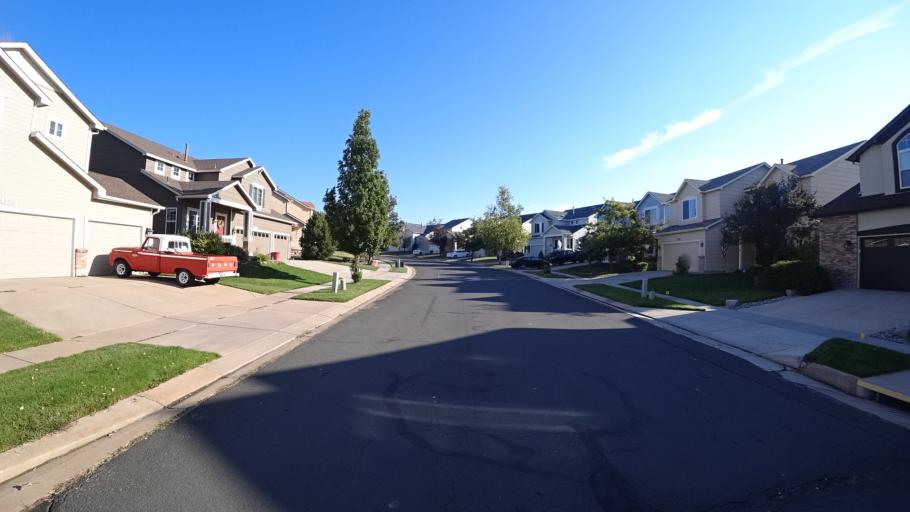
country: US
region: Colorado
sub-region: El Paso County
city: Cimarron Hills
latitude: 38.8908
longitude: -104.7029
